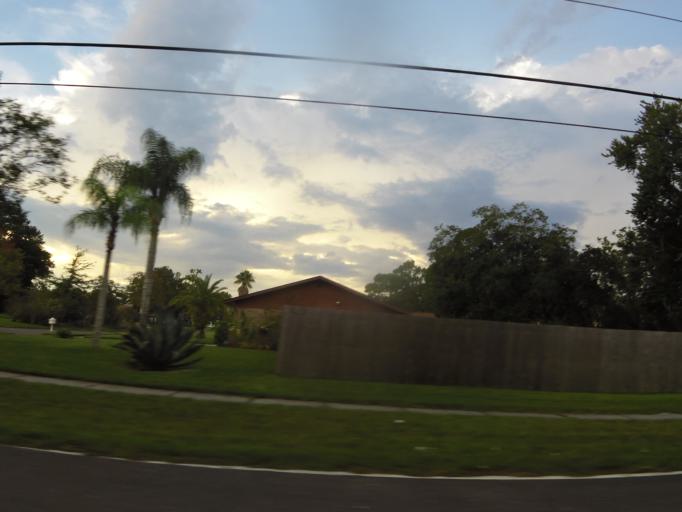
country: US
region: Florida
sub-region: Clay County
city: Bellair-Meadowbrook Terrace
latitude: 30.2667
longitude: -81.7814
